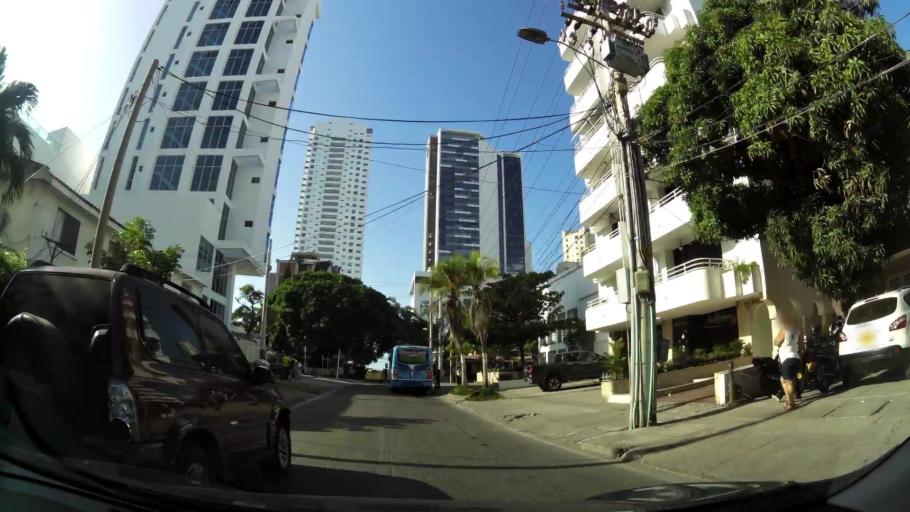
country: CO
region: Bolivar
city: Cartagena
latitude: 10.3984
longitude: -75.5582
